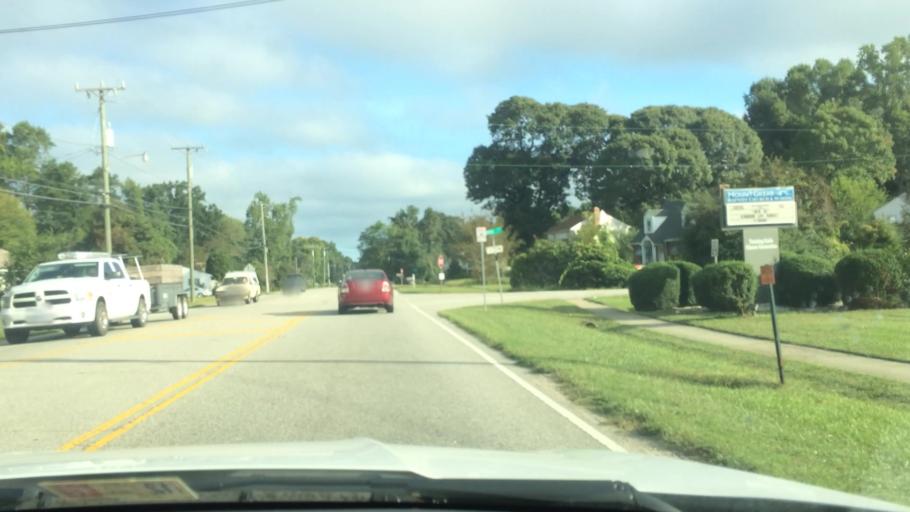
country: US
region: Virginia
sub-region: City of Williamsburg
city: Williamsburg
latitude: 37.2222
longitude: -76.6259
